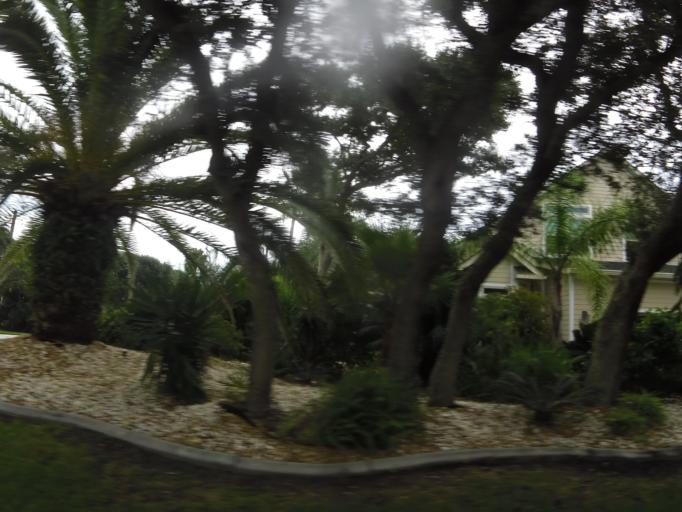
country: US
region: Florida
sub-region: Saint Johns County
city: Villano Beach
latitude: 29.9430
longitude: -81.3038
